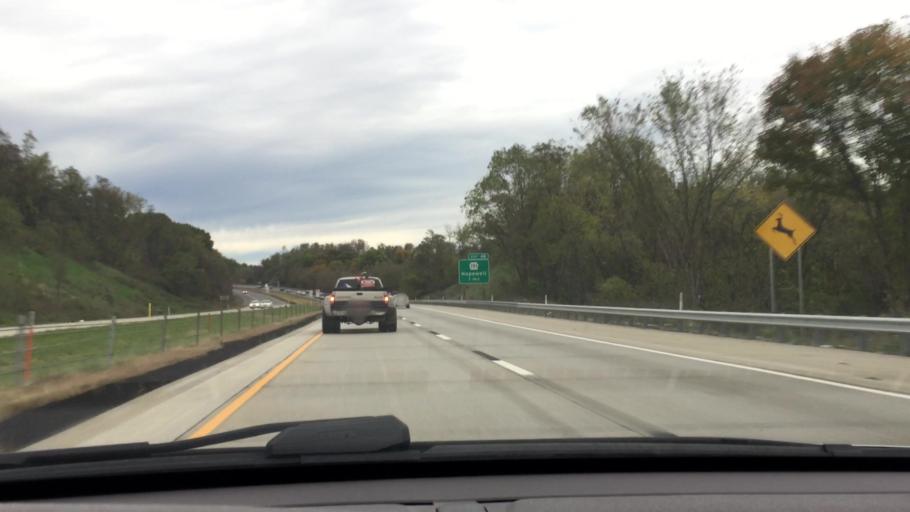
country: US
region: Pennsylvania
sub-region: Allegheny County
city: Carnot-Moon
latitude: 40.5394
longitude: -80.2722
